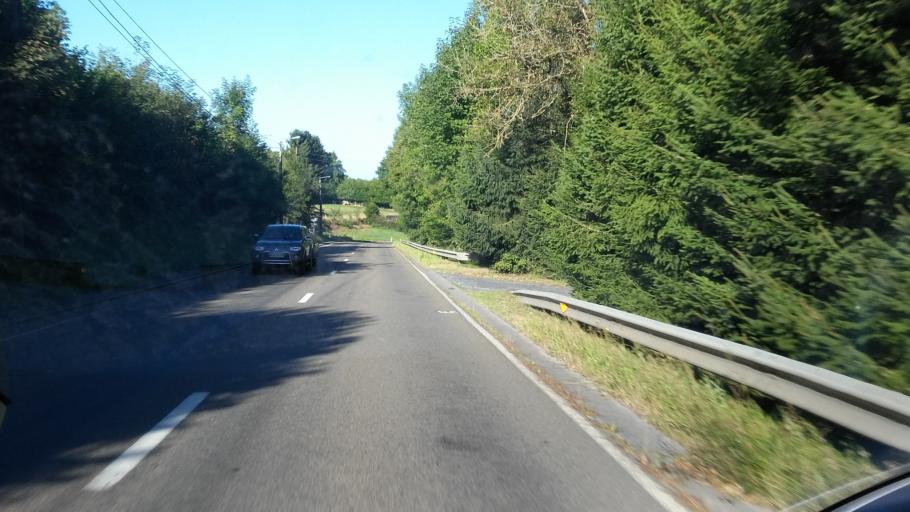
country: BE
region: Wallonia
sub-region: Province du Luxembourg
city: Neufchateau
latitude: 49.8381
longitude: 5.4515
